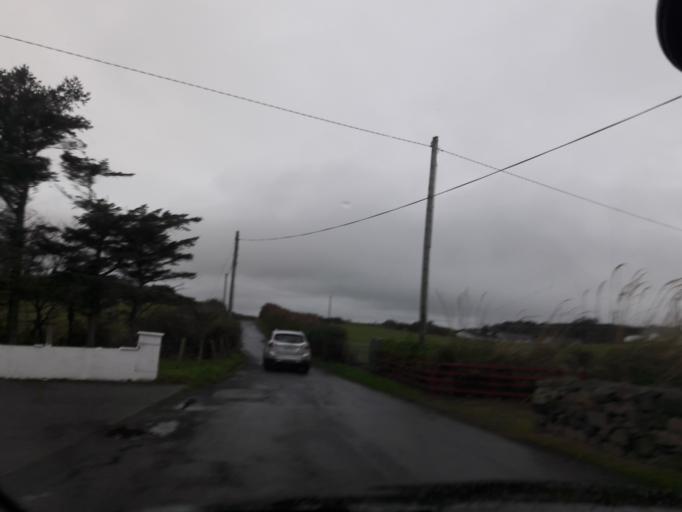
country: IE
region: Ulster
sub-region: County Donegal
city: Buncrana
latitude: 55.2499
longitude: -7.6240
